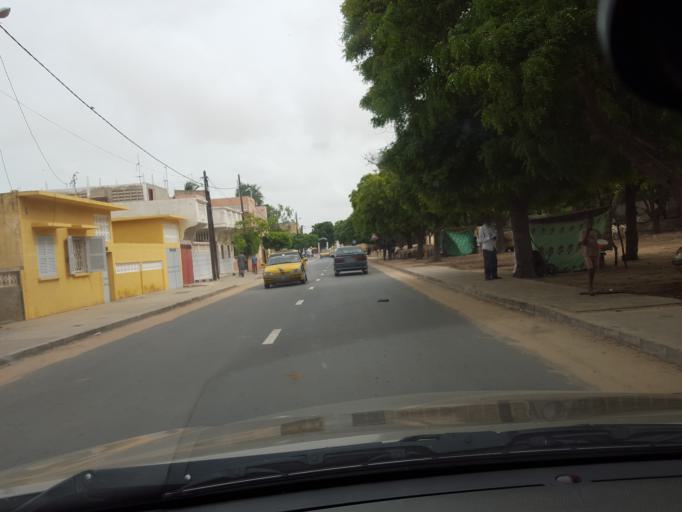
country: SN
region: Saint-Louis
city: Saint-Louis
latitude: 16.0305
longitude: -16.4888
